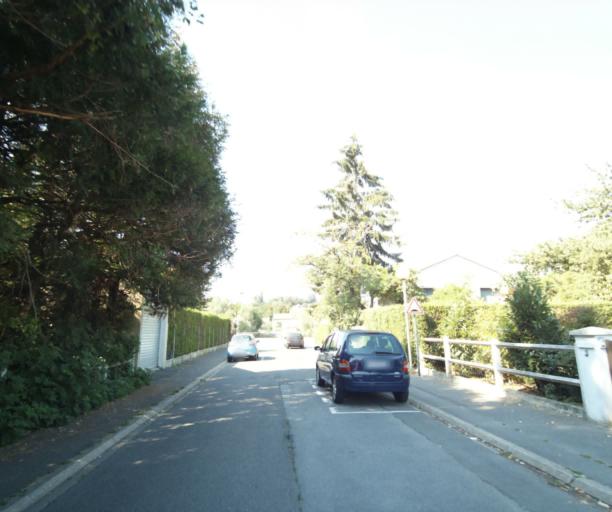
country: FR
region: Ile-de-France
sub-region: Departement de Seine-et-Marne
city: Pomponne
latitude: 48.8792
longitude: 2.6977
